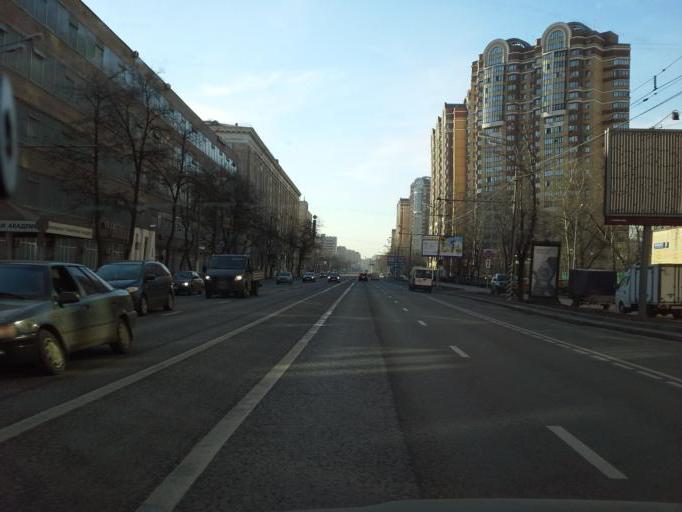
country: RU
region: Moscow
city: Taganskiy
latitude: 55.7370
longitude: 37.6936
